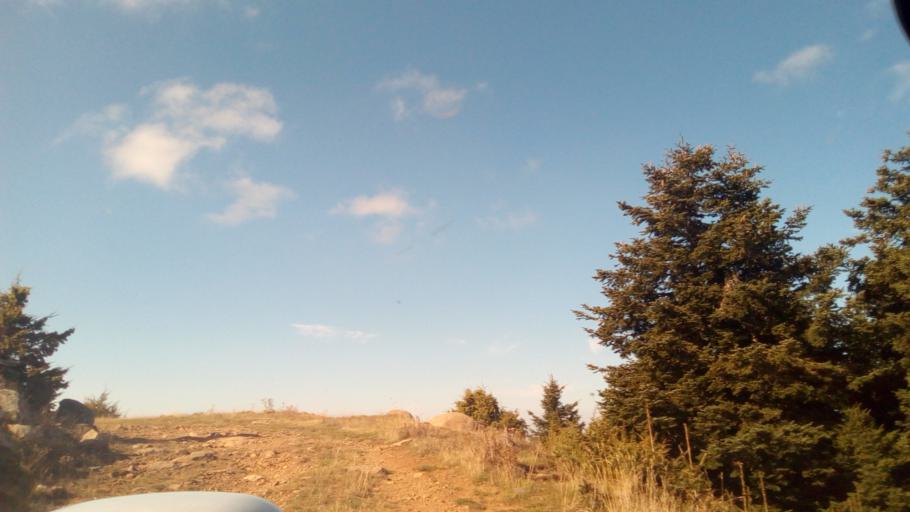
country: GR
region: Central Greece
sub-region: Nomos Fokidos
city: Lidoriki
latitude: 38.6086
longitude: 21.9651
